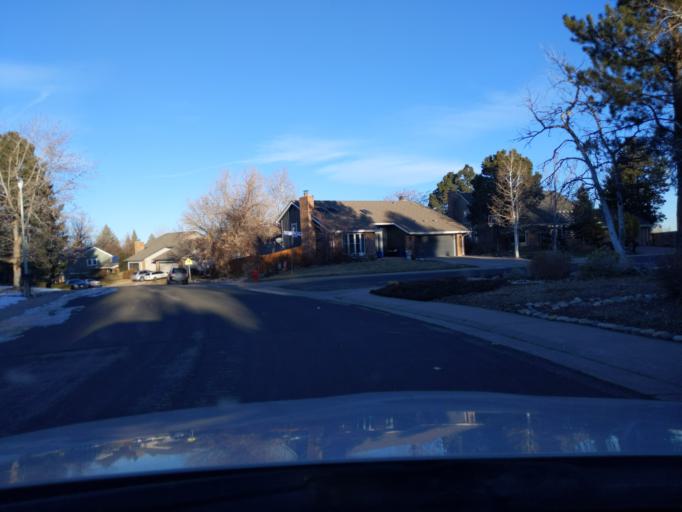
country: US
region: Colorado
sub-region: Arapahoe County
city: Centennial
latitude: 39.5725
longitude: -104.8876
